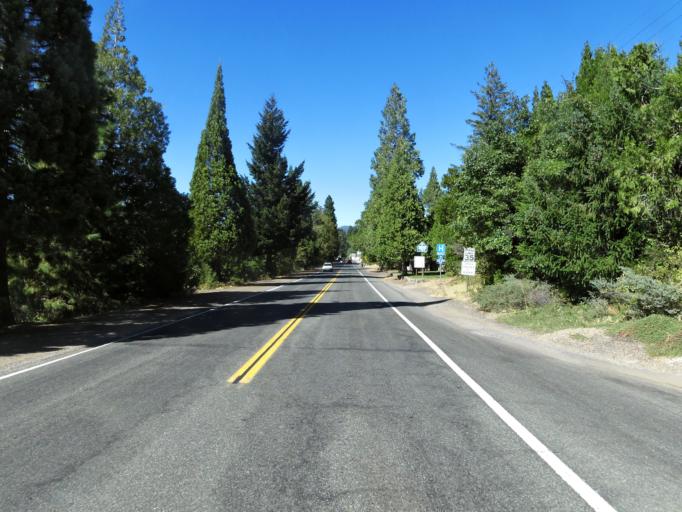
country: US
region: California
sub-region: Siskiyou County
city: Mount Shasta
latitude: 41.2984
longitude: -122.3062
